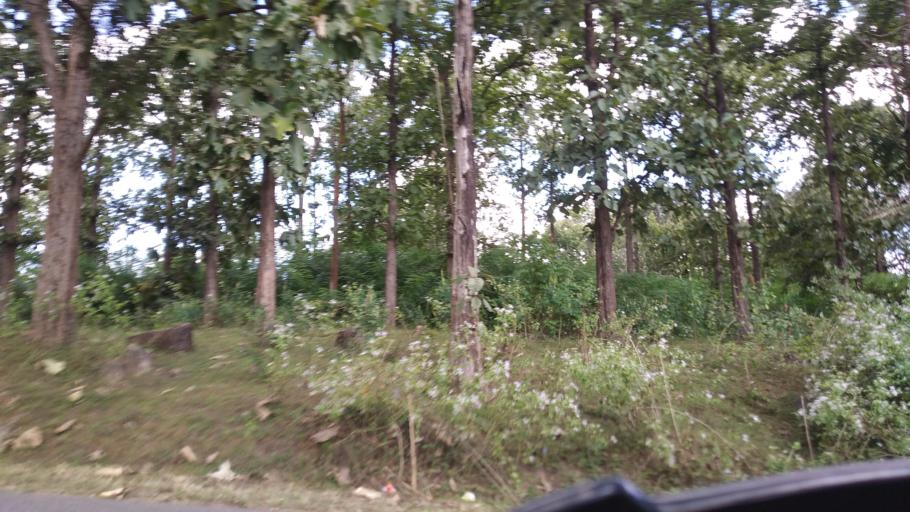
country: IN
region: Kerala
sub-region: Wayanad
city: Panamaram
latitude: 11.9389
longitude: 76.0643
